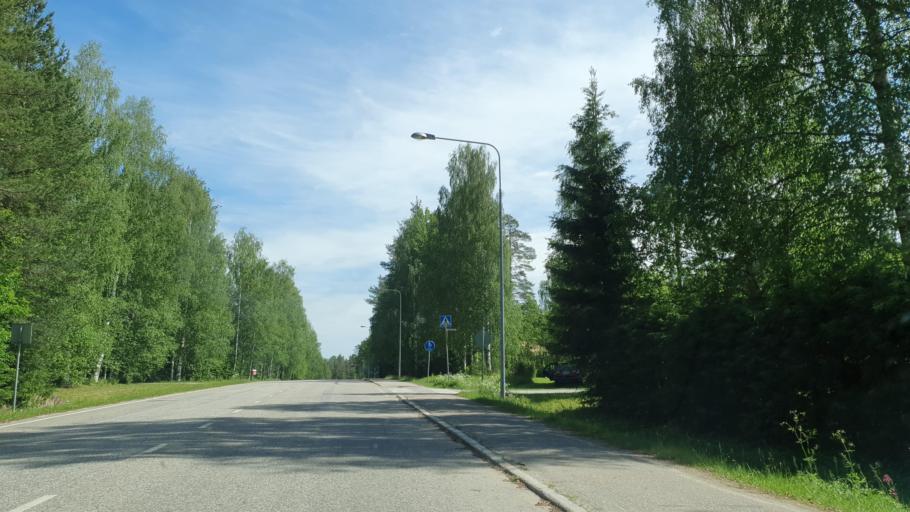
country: FI
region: Kainuu
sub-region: Kehys-Kainuu
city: Hyrynsalmi
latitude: 64.6829
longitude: 28.4654
